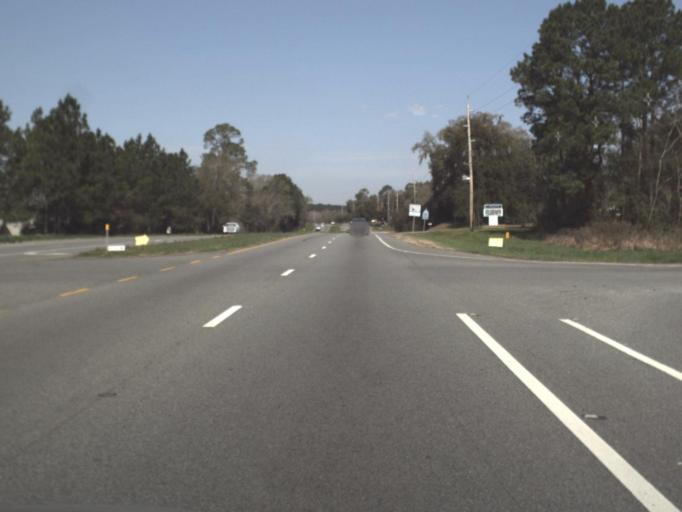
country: US
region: Florida
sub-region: Leon County
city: Tallahassee
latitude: 30.5145
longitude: -84.3452
